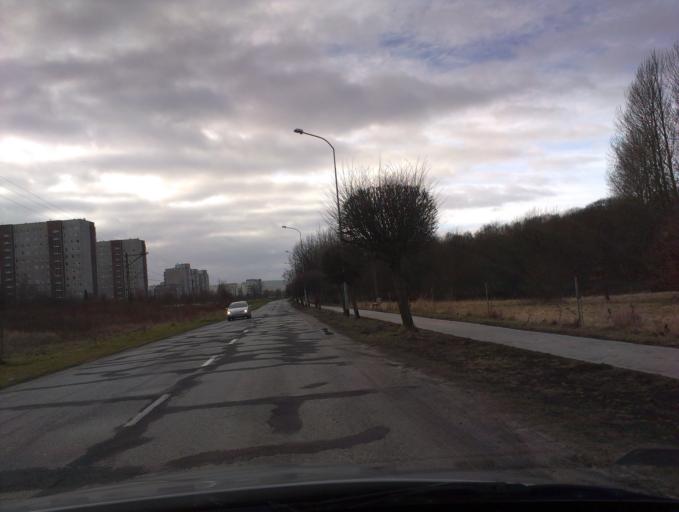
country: PL
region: West Pomeranian Voivodeship
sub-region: Powiat kolobrzeski
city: Kolobrzeg
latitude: 54.1831
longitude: 15.6015
